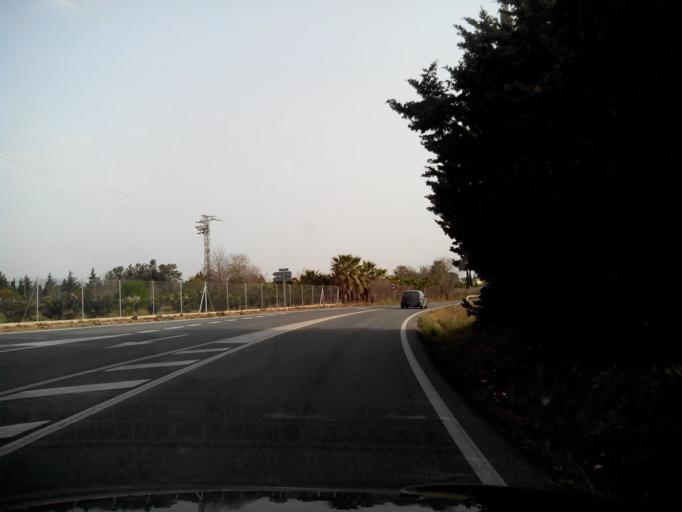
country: ES
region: Catalonia
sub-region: Provincia de Tarragona
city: Cambrils
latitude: 41.1052
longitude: 1.0842
